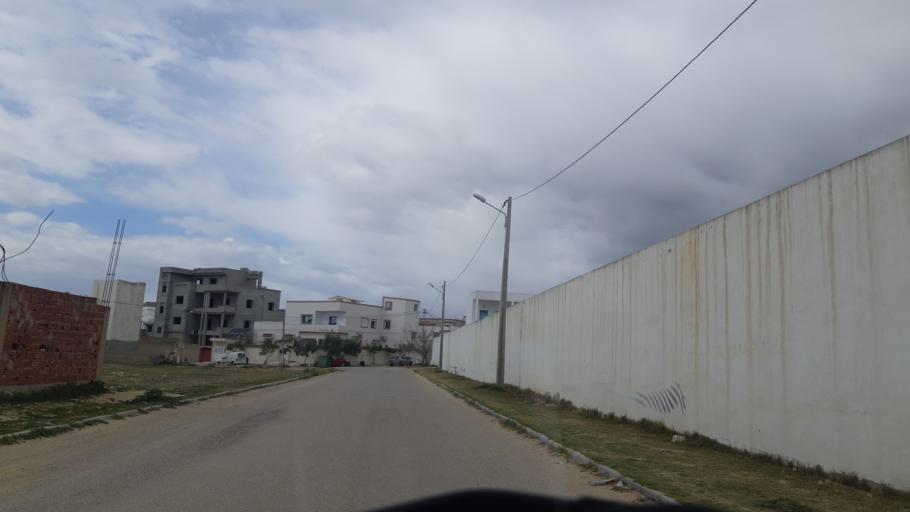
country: TN
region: Susah
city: Akouda
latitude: 35.8649
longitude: 10.5524
